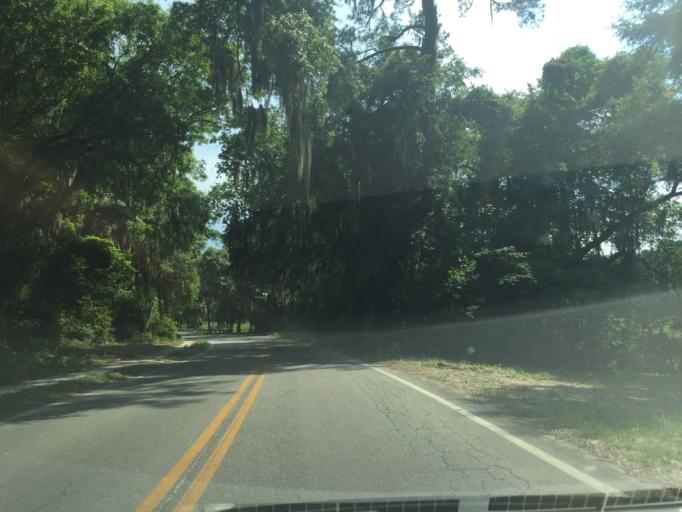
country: US
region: Georgia
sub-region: Chatham County
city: Isle of Hope
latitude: 31.9908
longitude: -81.1020
